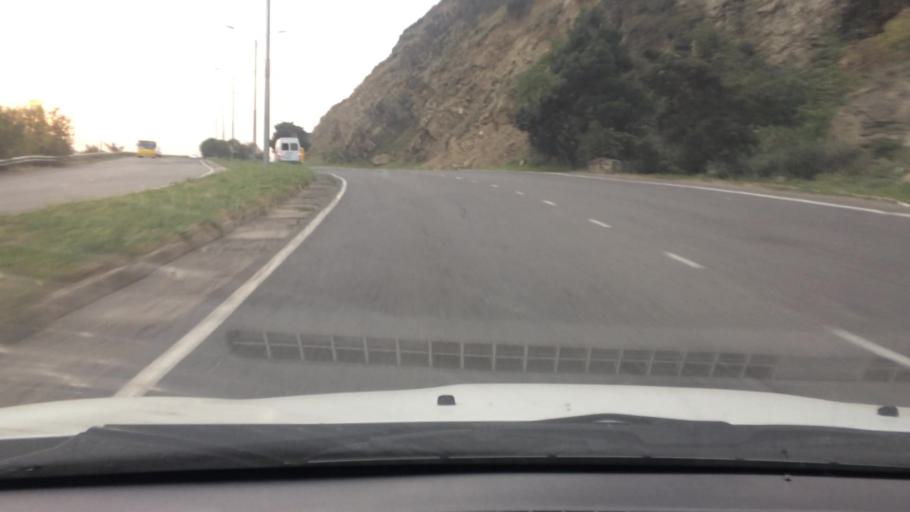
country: GE
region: T'bilisi
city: Tbilisi
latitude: 41.6583
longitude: 44.8906
